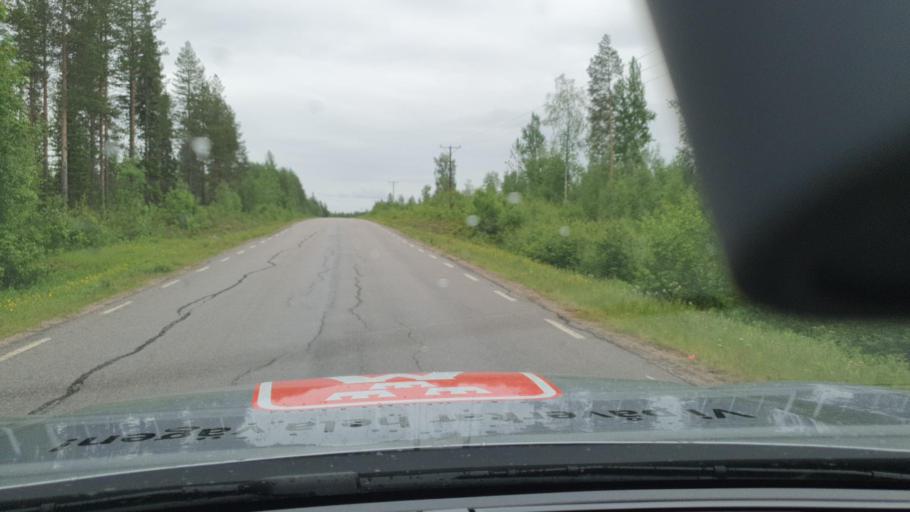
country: SE
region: Norrbotten
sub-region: Pajala Kommun
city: Pajala
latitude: 66.7506
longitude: 23.1627
